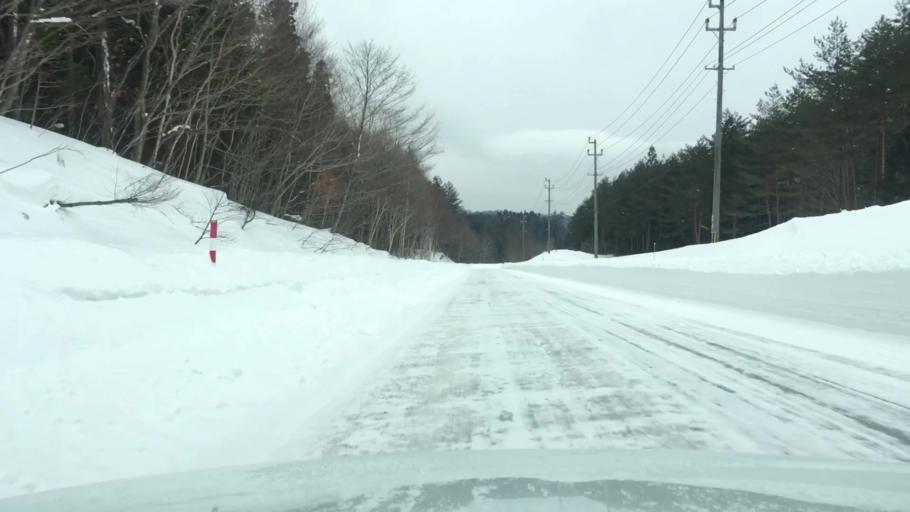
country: JP
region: Akita
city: Hanawa
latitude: 39.9872
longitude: 140.9997
